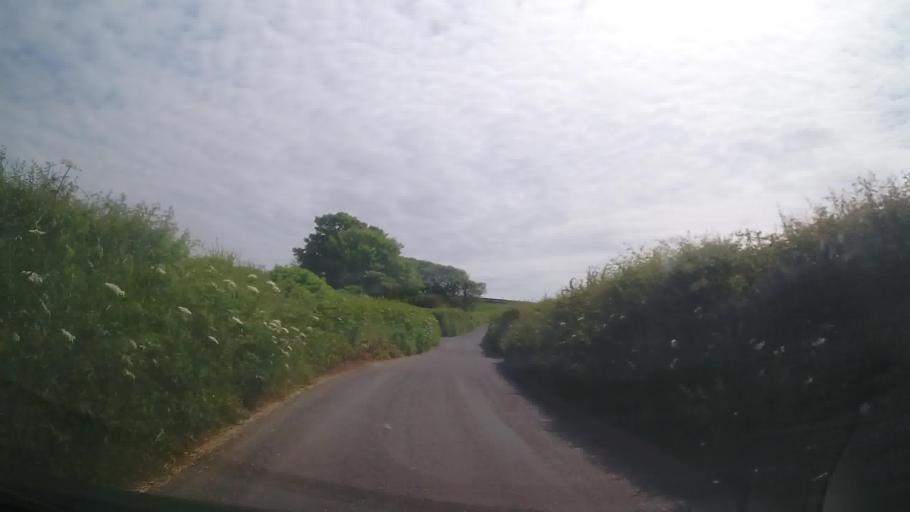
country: GB
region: England
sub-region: Devon
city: Salcombe
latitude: 50.2583
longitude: -3.6773
